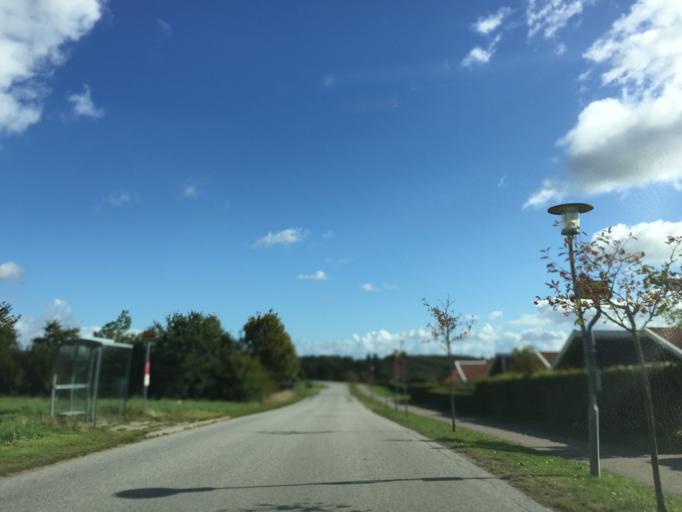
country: DK
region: Central Jutland
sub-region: Viborg Kommune
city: Viborg
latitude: 56.4454
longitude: 9.4458
